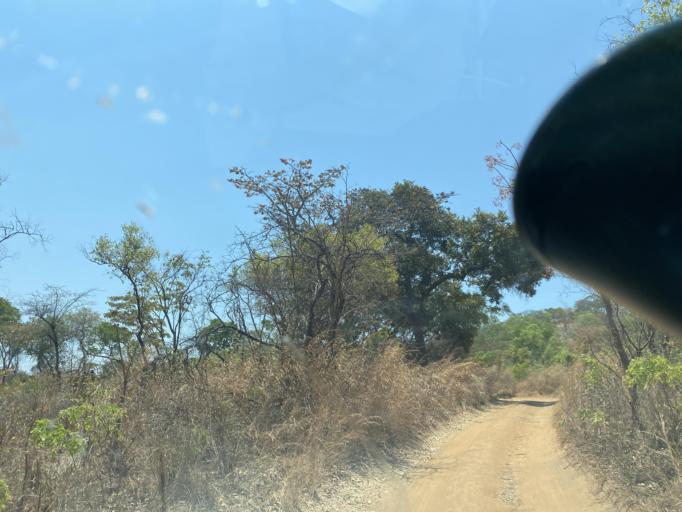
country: ZM
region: Lusaka
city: Chongwe
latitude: -15.4414
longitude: 29.2049
